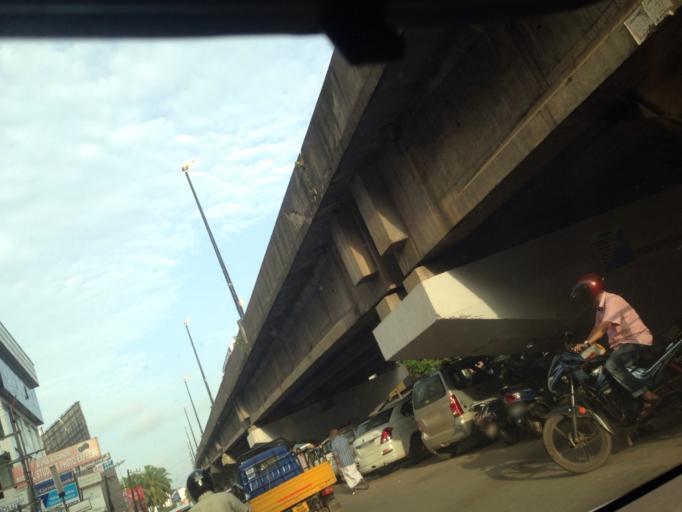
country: IN
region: Kerala
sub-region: Kozhikode
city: Kozhikode
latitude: 11.2593
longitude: 75.7902
